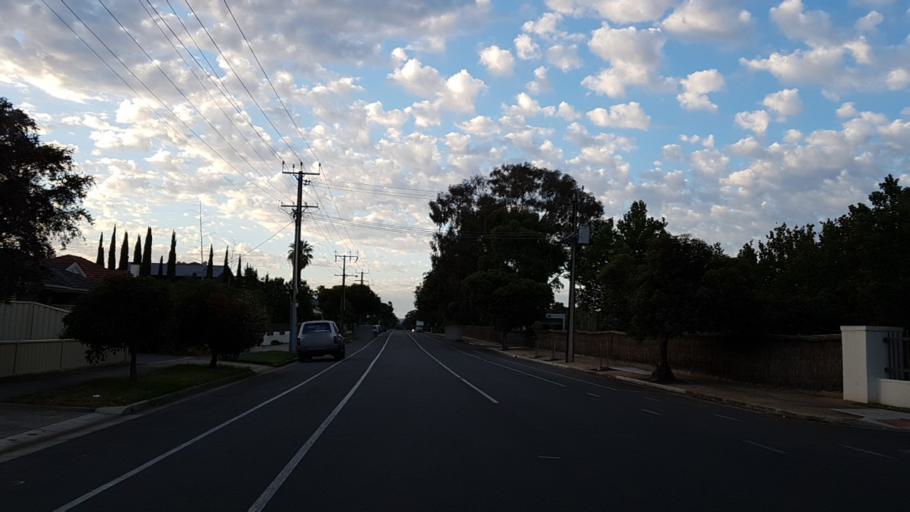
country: AU
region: South Australia
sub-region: City of West Torrens
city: Plympton
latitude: -34.9277
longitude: 138.5342
